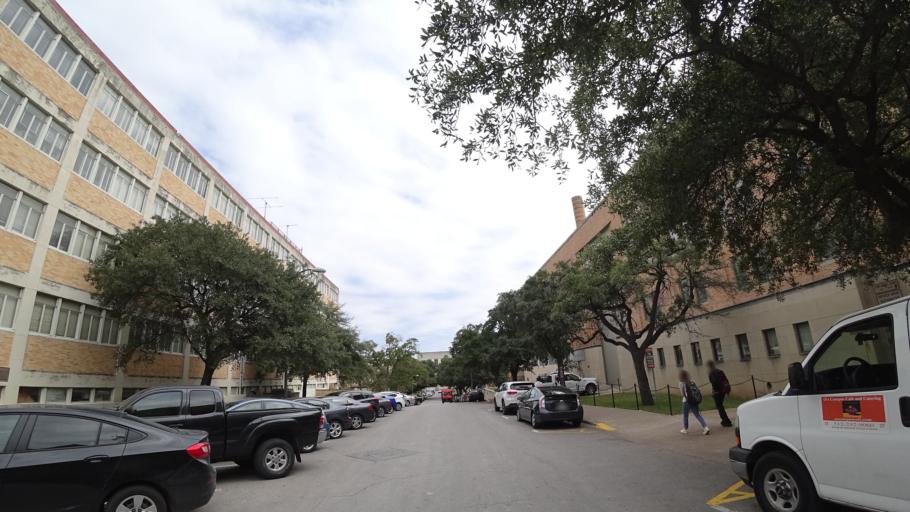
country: US
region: Texas
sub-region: Travis County
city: Austin
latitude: 30.2873
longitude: -97.7362
